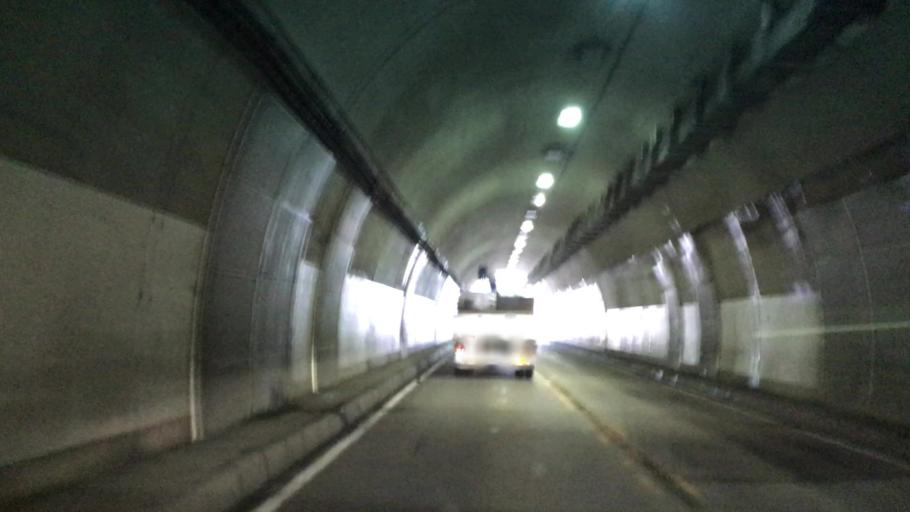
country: JP
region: Hokkaido
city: Iwanai
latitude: 43.1093
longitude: 140.4515
